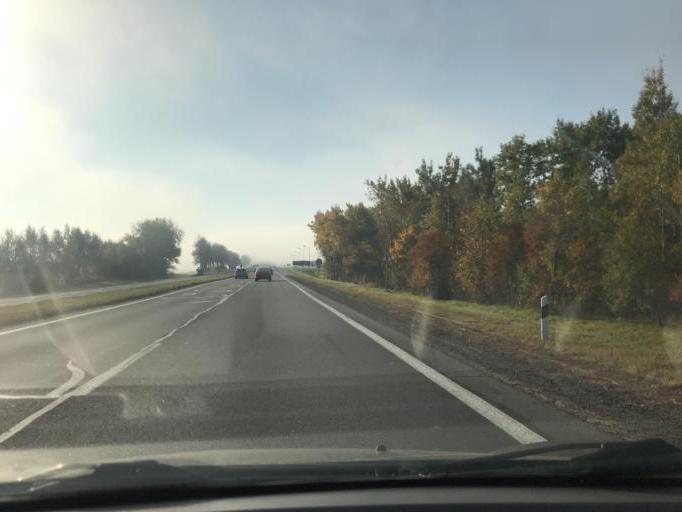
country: BY
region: Minsk
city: Luhavaya Slabada
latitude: 53.7605
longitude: 27.8291
